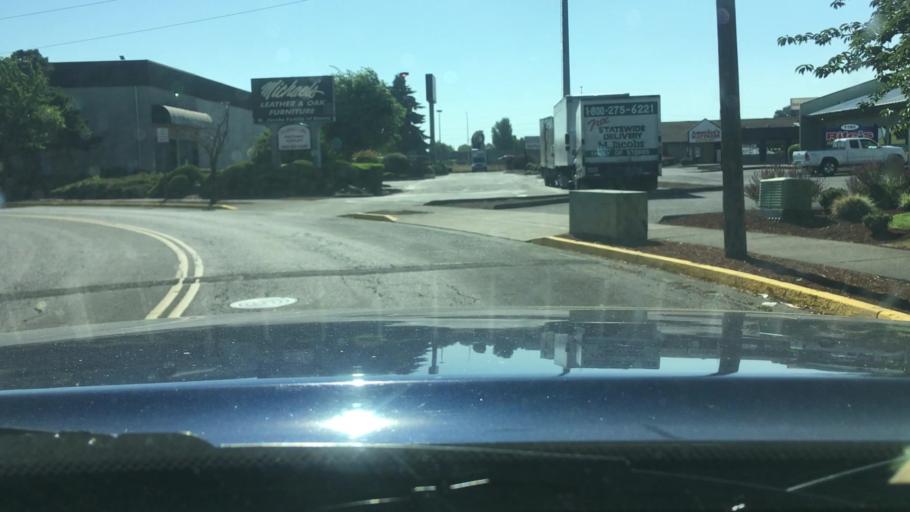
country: US
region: Oregon
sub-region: Lane County
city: Springfield
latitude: 44.0800
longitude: -123.0446
